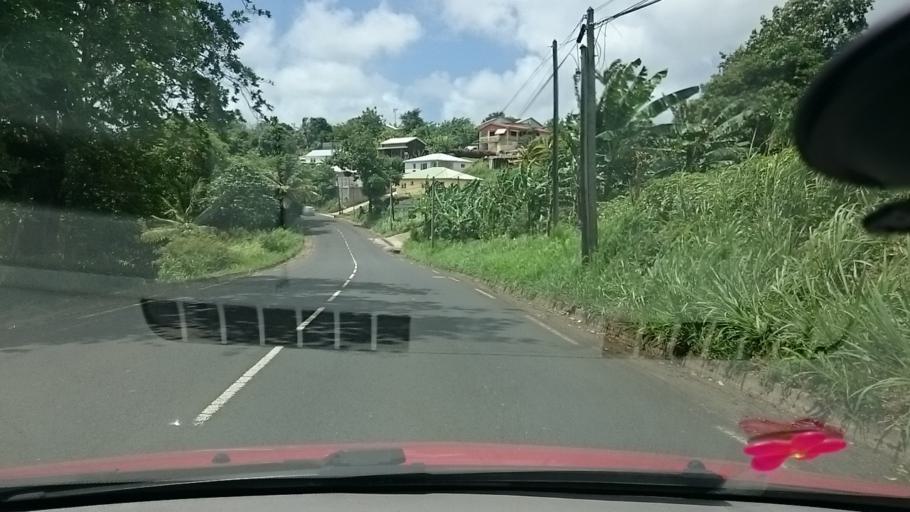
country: MQ
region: Martinique
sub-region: Martinique
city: Le Francois
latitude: 14.5951
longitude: -60.9247
